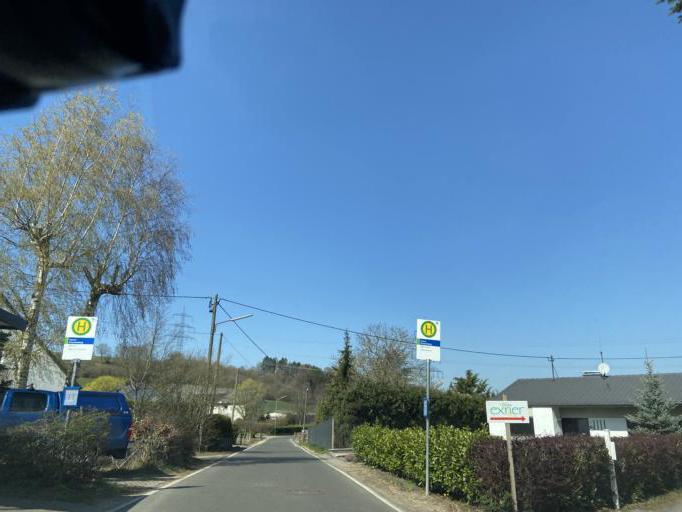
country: DE
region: Rheinland-Pfalz
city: Newel
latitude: 49.7966
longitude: 6.5846
